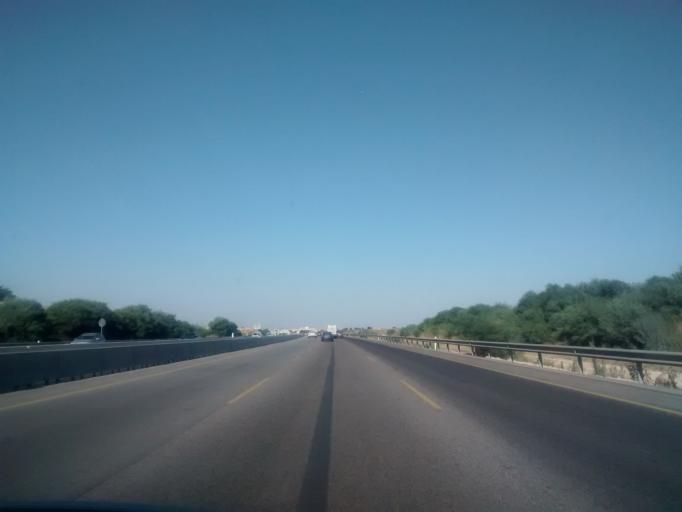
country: ES
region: Andalusia
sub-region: Provincia de Sevilla
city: Espartinas
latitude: 37.3641
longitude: -6.1222
